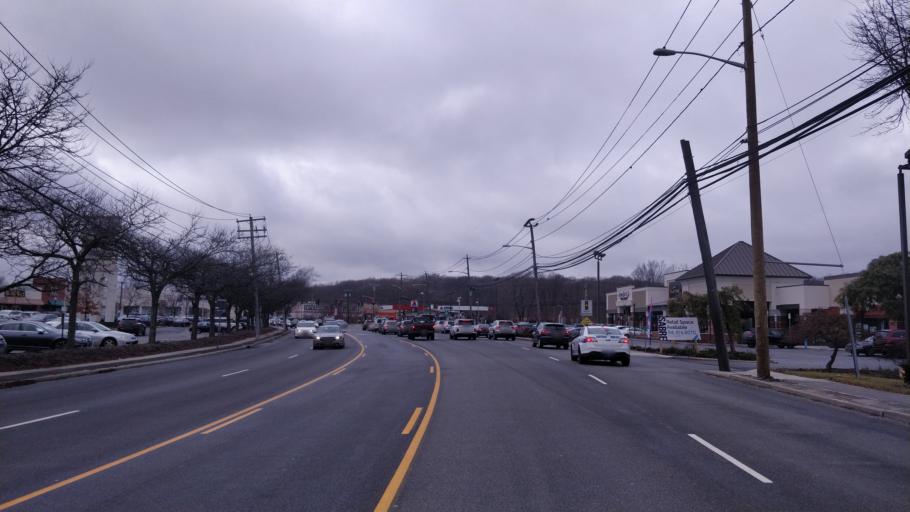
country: US
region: New York
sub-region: Suffolk County
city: Elwood
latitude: 40.8384
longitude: -73.3309
